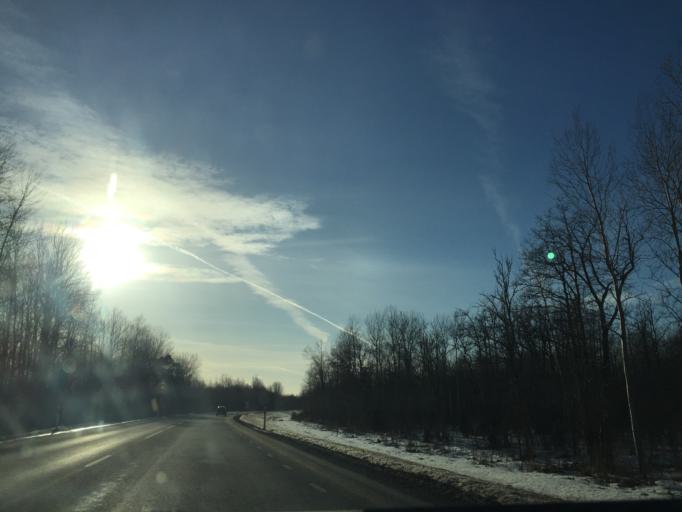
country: EE
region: Saare
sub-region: Kuressaare linn
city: Kuressaare
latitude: 58.3172
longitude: 22.6241
